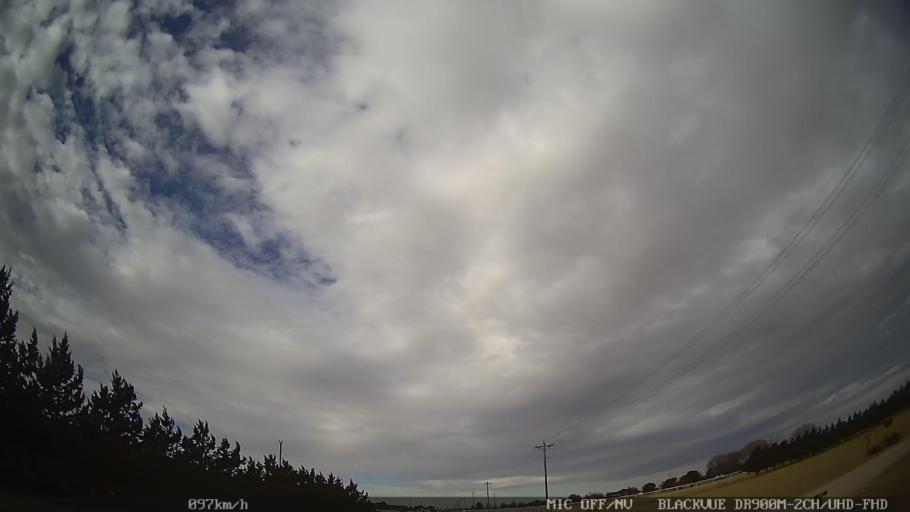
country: US
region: New Mexico
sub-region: Curry County
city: Texico
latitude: 34.4191
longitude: -103.0999
